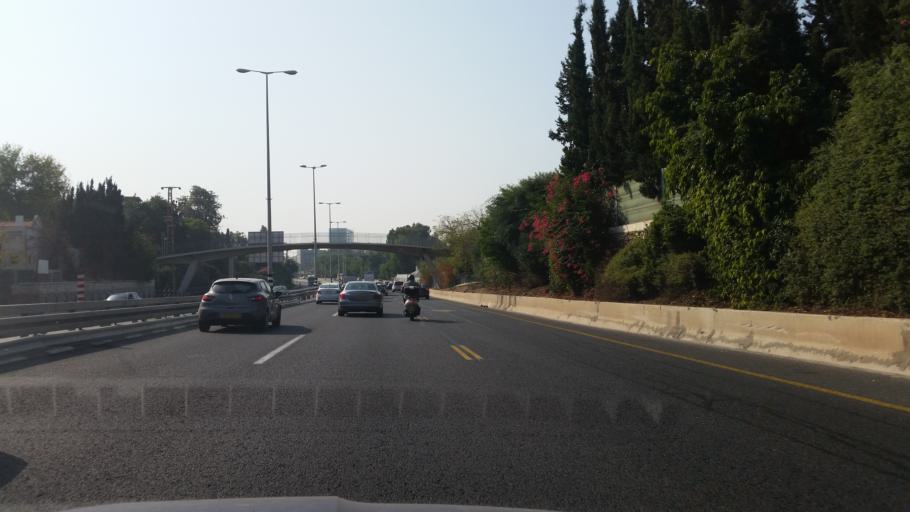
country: IL
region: Tel Aviv
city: Herzliyya
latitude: 32.1728
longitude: 34.8150
